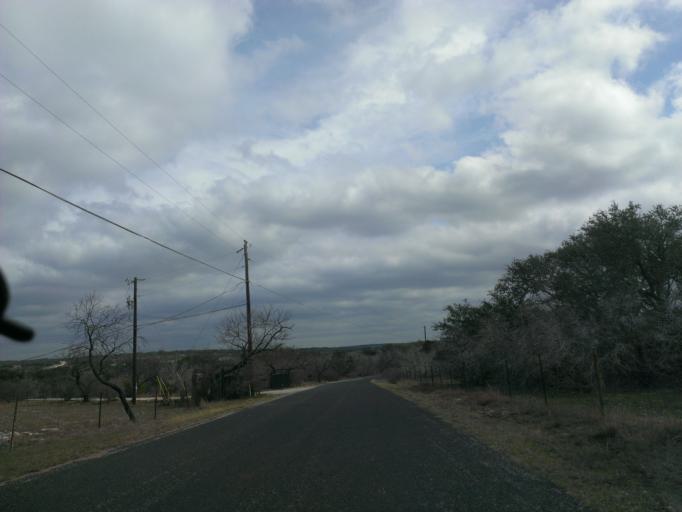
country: US
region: Texas
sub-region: Travis County
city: Briarcliff
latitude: 30.3932
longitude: -98.1038
